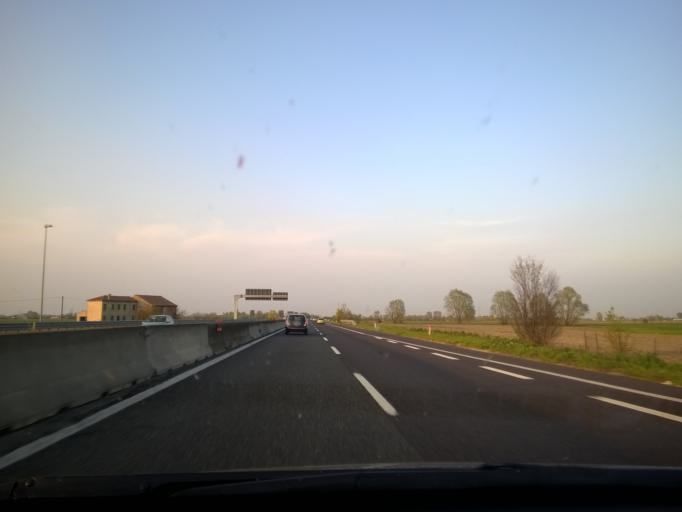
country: IT
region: Veneto
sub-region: Provincia di Rovigo
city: Villamarzana
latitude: 45.0266
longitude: 11.6979
